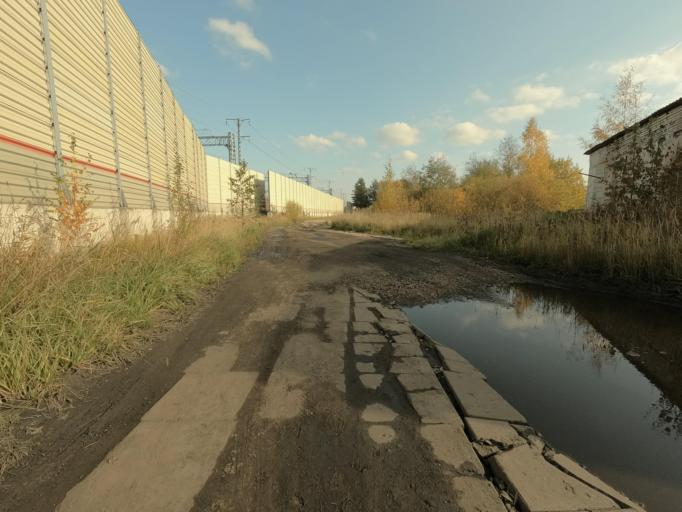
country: RU
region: Leningrad
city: Mga
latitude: 59.7545
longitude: 31.0651
